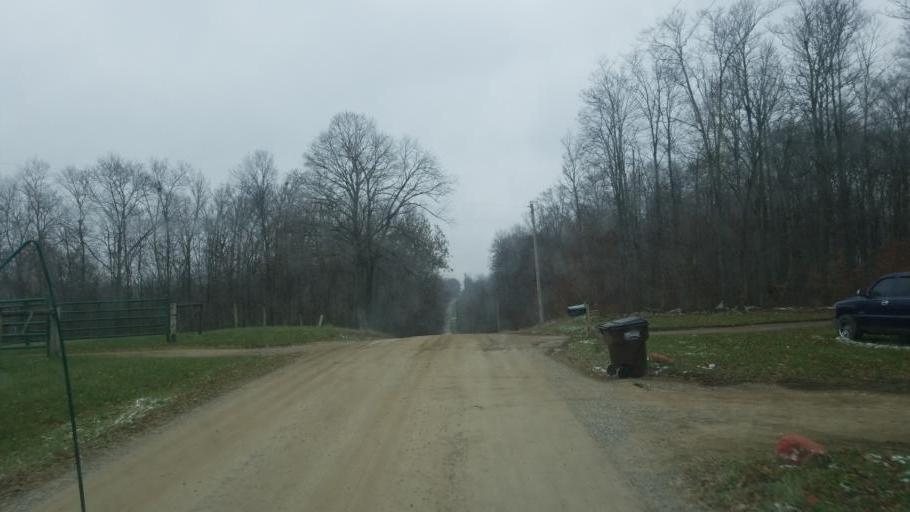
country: US
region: Ohio
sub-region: Huron County
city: New London
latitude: 40.9753
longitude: -82.3856
